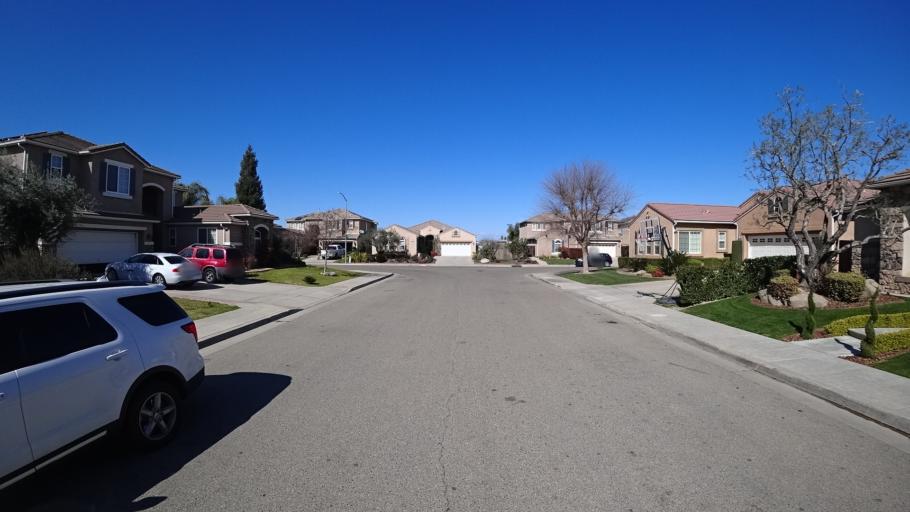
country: US
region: California
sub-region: Fresno County
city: Clovis
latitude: 36.8624
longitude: -119.7318
